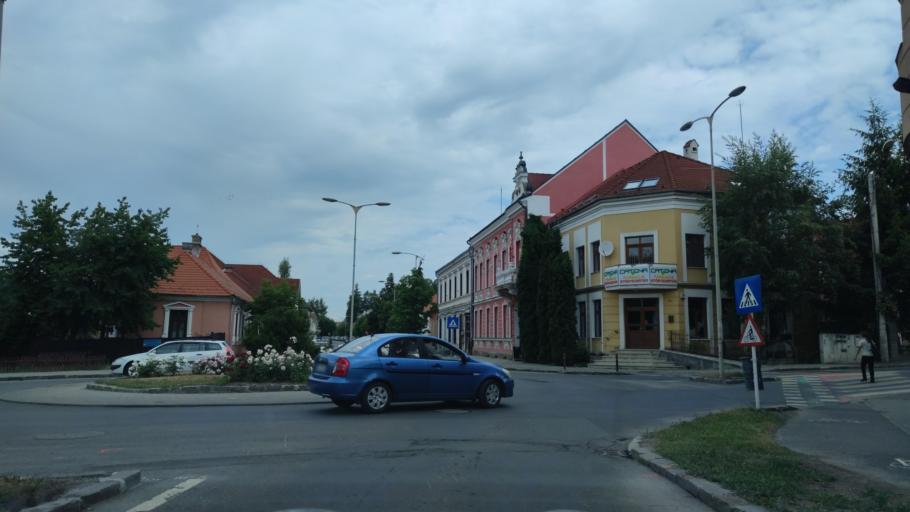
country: RO
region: Harghita
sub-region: Municipiul Miercurea Ciuc
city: Miercurea-Ciuc
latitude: 46.3640
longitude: 25.8063
